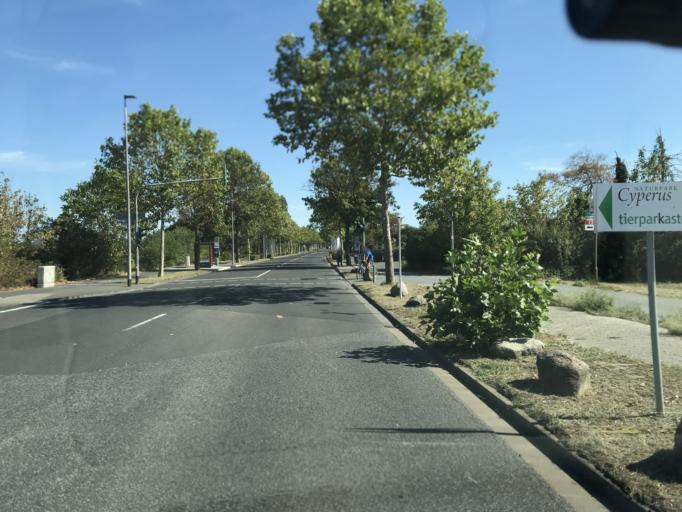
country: DE
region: Rheinland-Pfalz
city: Mainz
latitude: 50.0239
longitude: 8.2775
